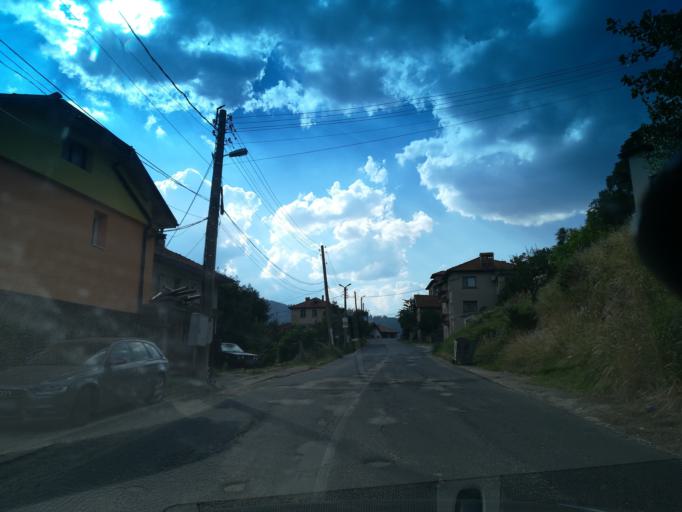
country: BG
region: Smolyan
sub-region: Obshtina Smolyan
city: Smolyan
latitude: 41.6559
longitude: 24.7694
